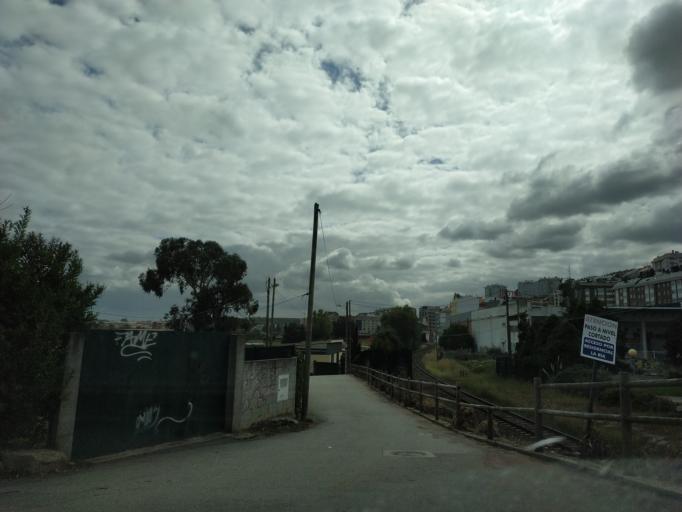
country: ES
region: Galicia
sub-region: Provincia da Coruna
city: Culleredo
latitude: 43.3277
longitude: -8.3808
